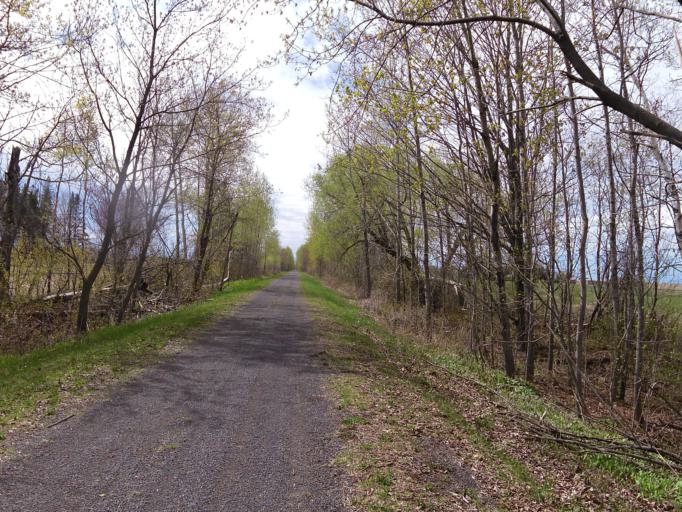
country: CA
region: Ontario
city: Hawkesbury
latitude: 45.5390
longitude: -74.7332
